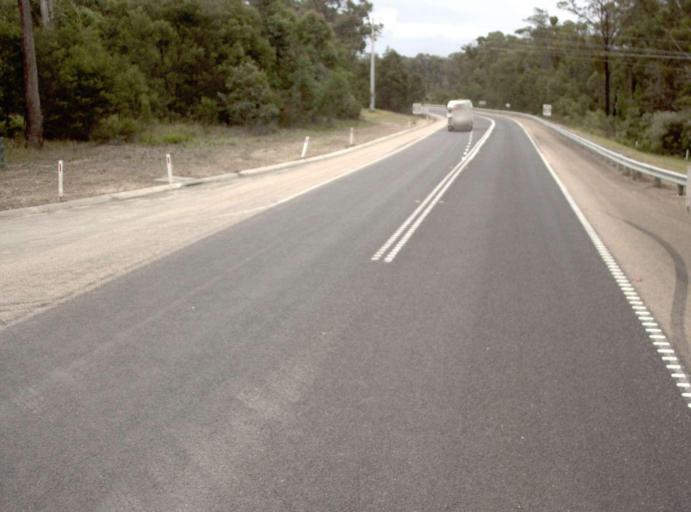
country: AU
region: Victoria
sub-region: East Gippsland
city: Lakes Entrance
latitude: -37.7248
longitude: 148.0873
